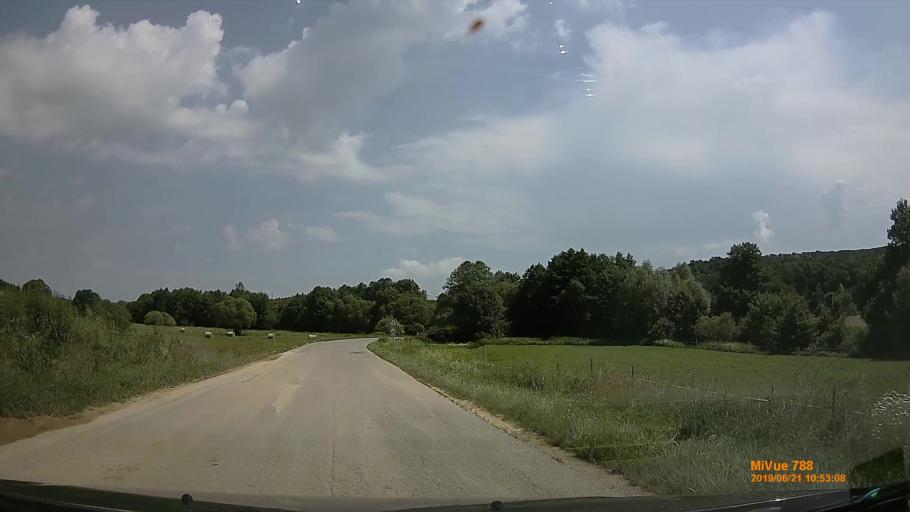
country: HU
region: Baranya
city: Buekkoesd
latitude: 46.1420
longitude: 18.0594
